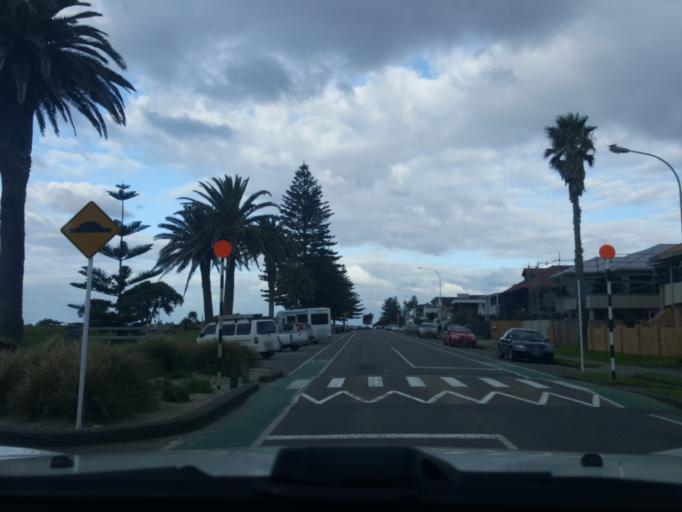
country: NZ
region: Bay of Plenty
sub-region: Tauranga City
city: Tauranga
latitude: -37.6347
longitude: 176.1852
